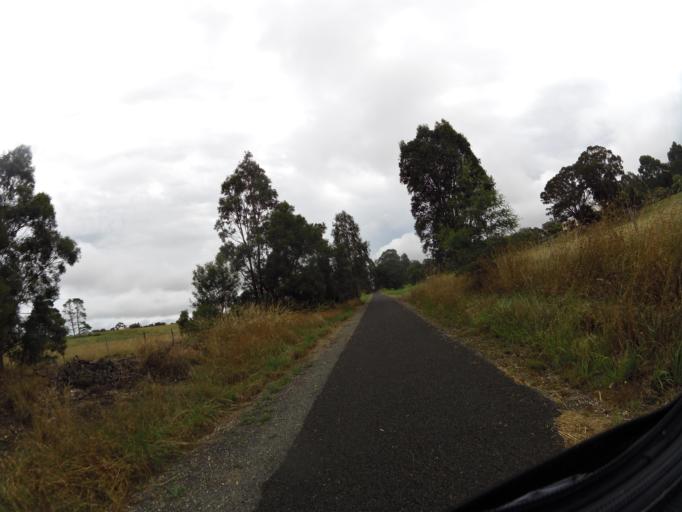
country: AU
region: Victoria
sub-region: East Gippsland
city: Bairnsdale
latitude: -37.8191
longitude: 147.7232
